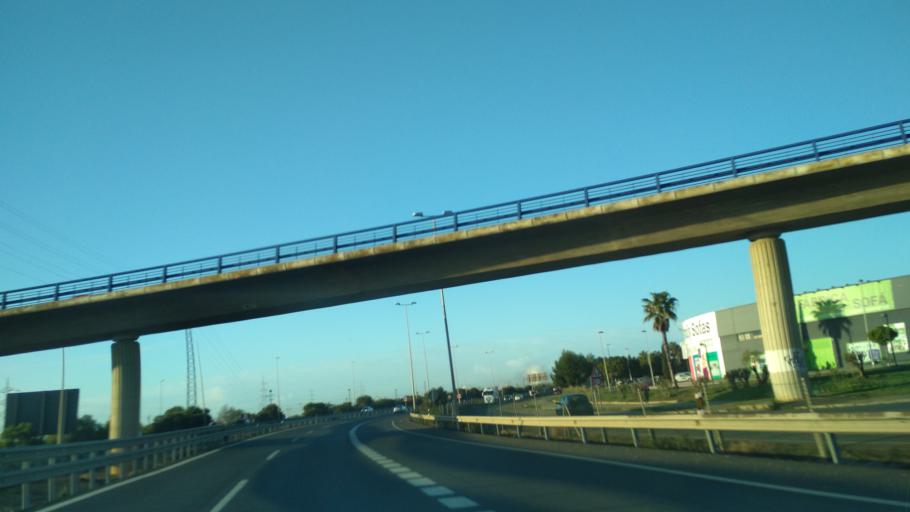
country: ES
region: Andalusia
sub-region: Provincia de Huelva
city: Huelva
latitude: 37.2606
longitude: -6.9203
